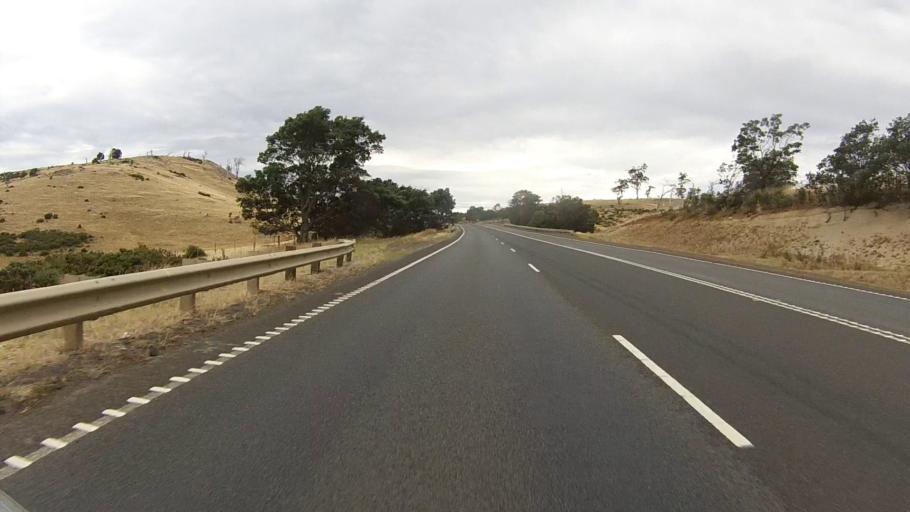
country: AU
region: Tasmania
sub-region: Brighton
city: Bridgewater
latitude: -42.3404
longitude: 147.3407
